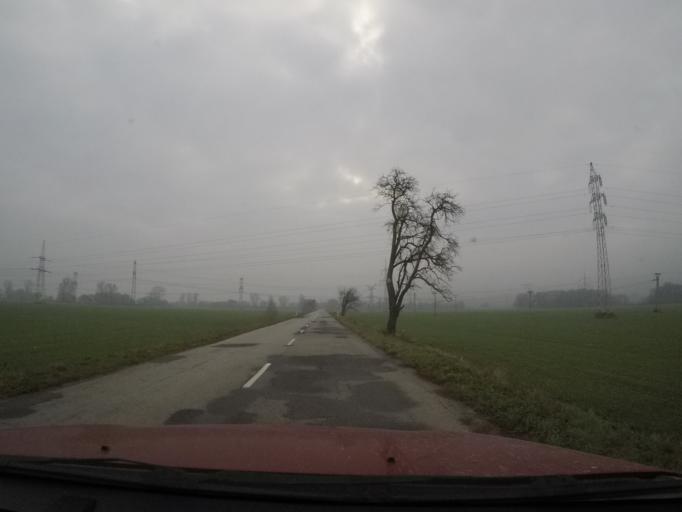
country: SK
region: Presovsky
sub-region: Okres Presov
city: Presov
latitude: 48.8657
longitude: 21.2710
